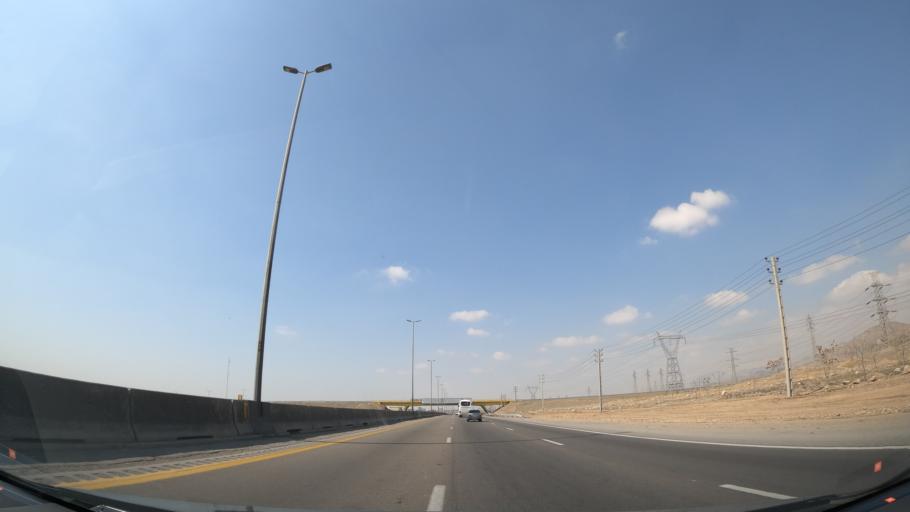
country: IR
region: Qazvin
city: Abyek
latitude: 36.0634
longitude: 50.4923
